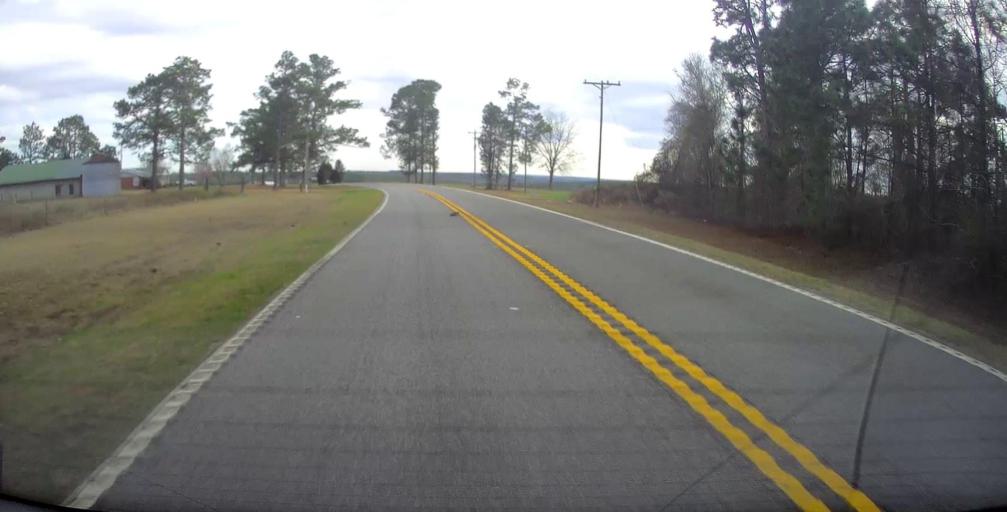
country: US
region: Georgia
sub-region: Marion County
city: Buena Vista
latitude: 32.4450
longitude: -84.4404
